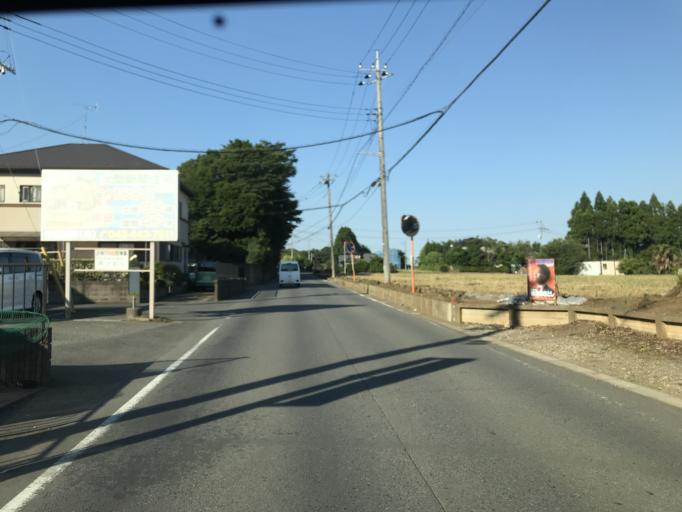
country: JP
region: Chiba
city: Yachimata
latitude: 35.6007
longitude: 140.2625
